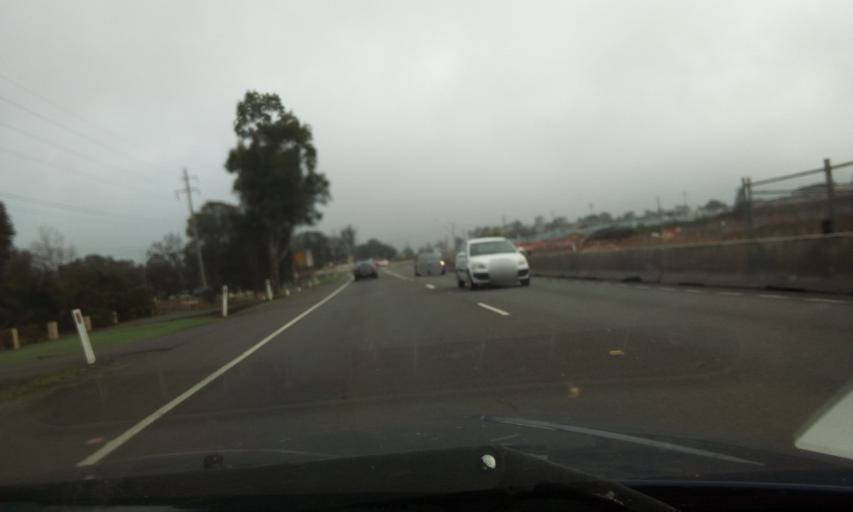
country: AU
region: New South Wales
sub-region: Penrith Municipality
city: Glenmore Park
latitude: -33.7959
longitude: 150.6986
